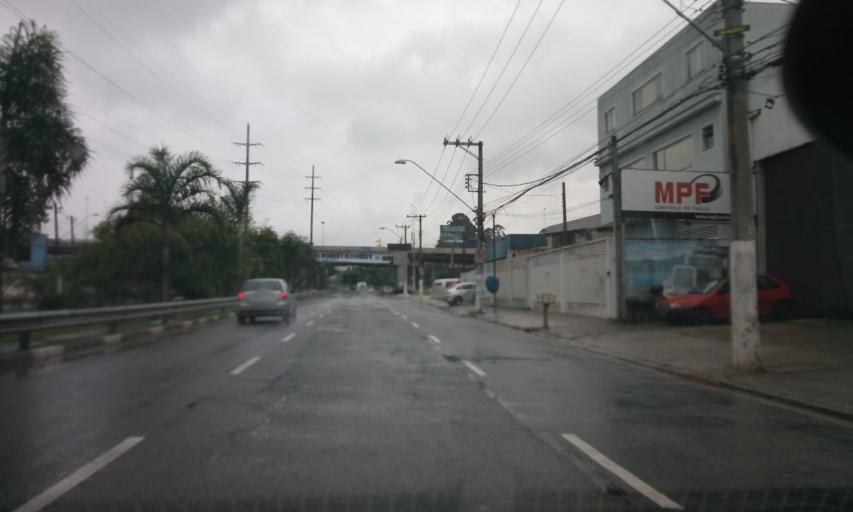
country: BR
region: Sao Paulo
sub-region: Sao Bernardo Do Campo
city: Sao Bernardo do Campo
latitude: -23.7103
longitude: -46.5745
